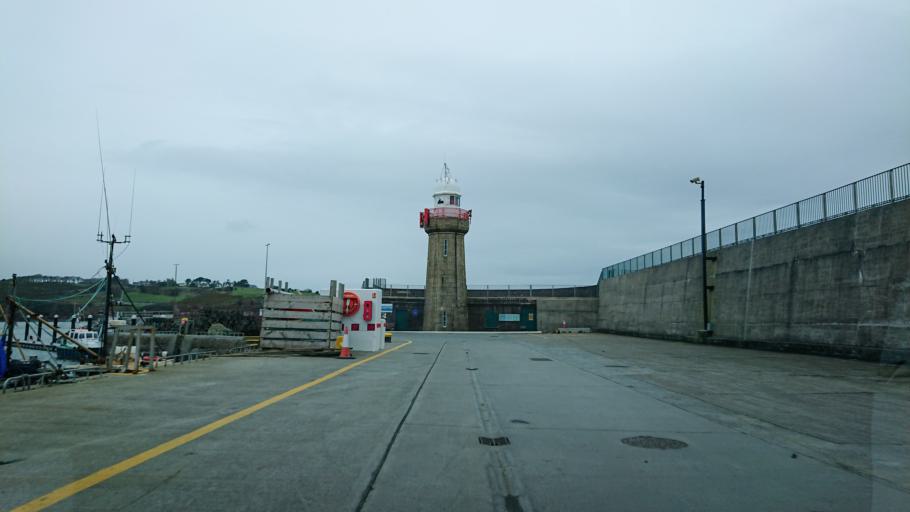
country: IE
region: Munster
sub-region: Waterford
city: Dunmore East
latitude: 52.1483
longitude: -6.9896
